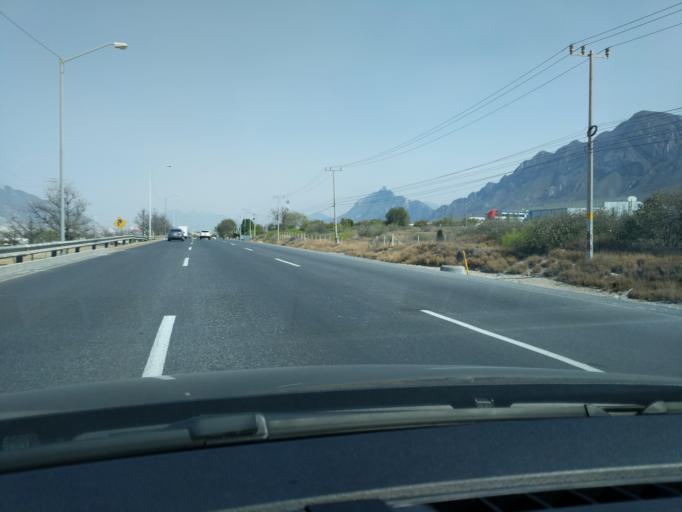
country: MX
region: Nuevo Leon
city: Santa Catarina
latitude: 25.6920
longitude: -100.5084
